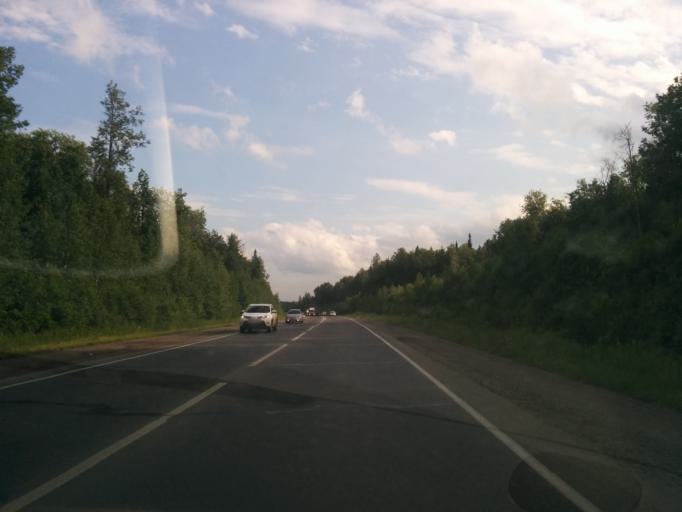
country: RU
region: Perm
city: Novyye Lyady
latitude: 58.1002
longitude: 56.4249
